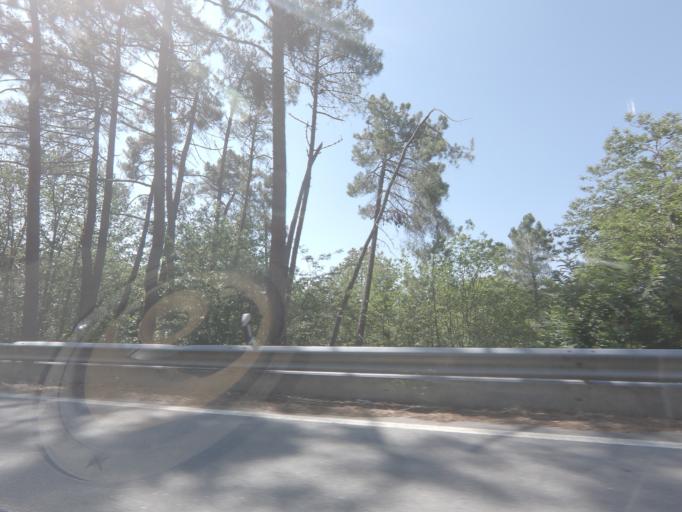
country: PT
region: Viseu
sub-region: Tarouca
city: Tarouca
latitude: 41.0343
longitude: -7.7447
